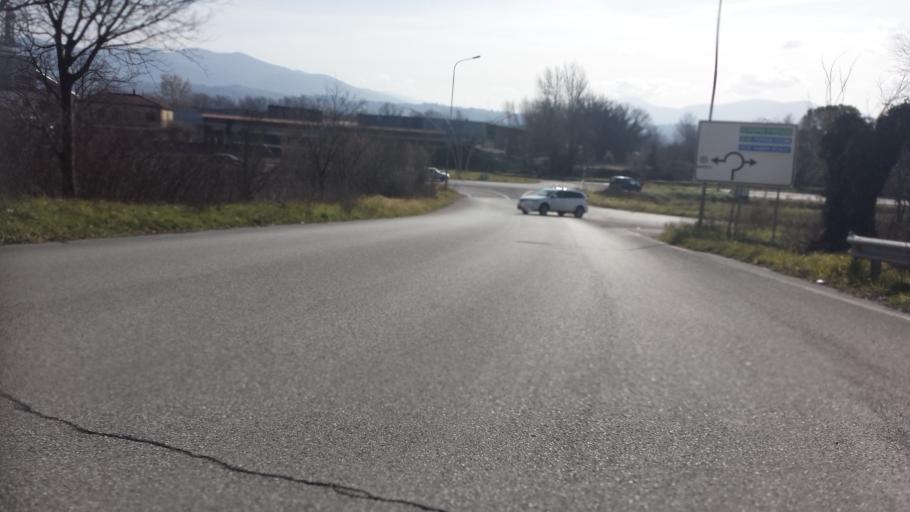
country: IT
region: Umbria
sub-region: Provincia di Terni
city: Terni
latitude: 42.5679
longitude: 12.5980
